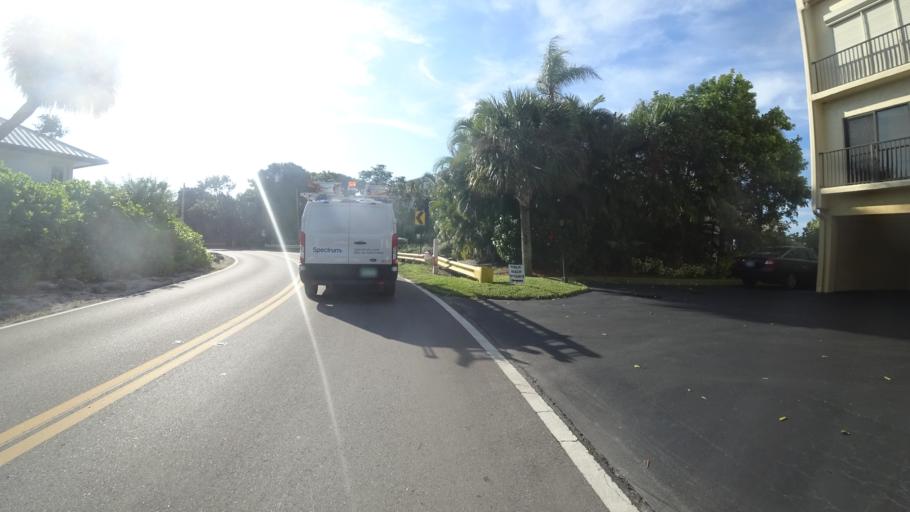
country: US
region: Florida
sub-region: Manatee County
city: Holmes Beach
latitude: 27.5084
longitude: -82.7192
